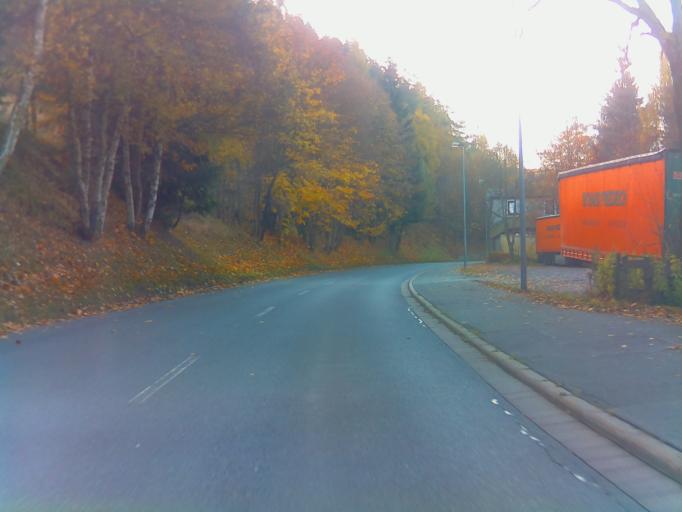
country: DE
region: Thuringia
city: Piesau
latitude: 50.5189
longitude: 11.2238
